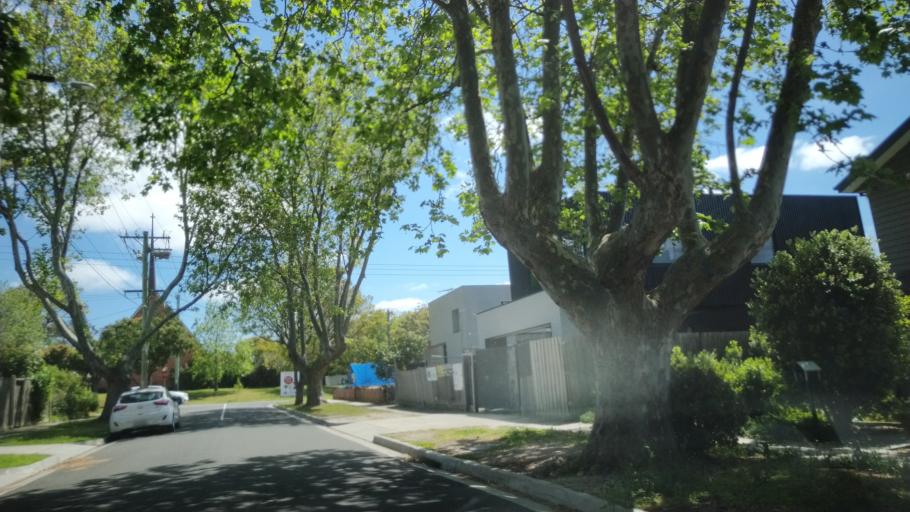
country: AU
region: Victoria
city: Hughesdale
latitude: -37.9025
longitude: 145.0760
